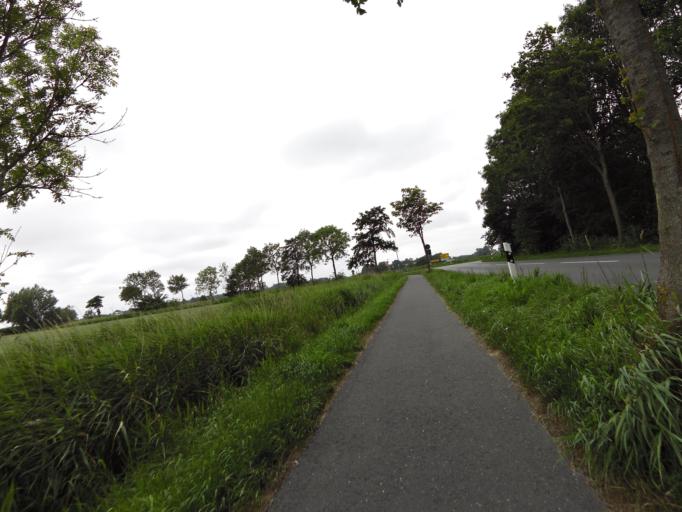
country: DE
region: Lower Saxony
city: Padingbuttel
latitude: 53.7185
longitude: 8.5453
